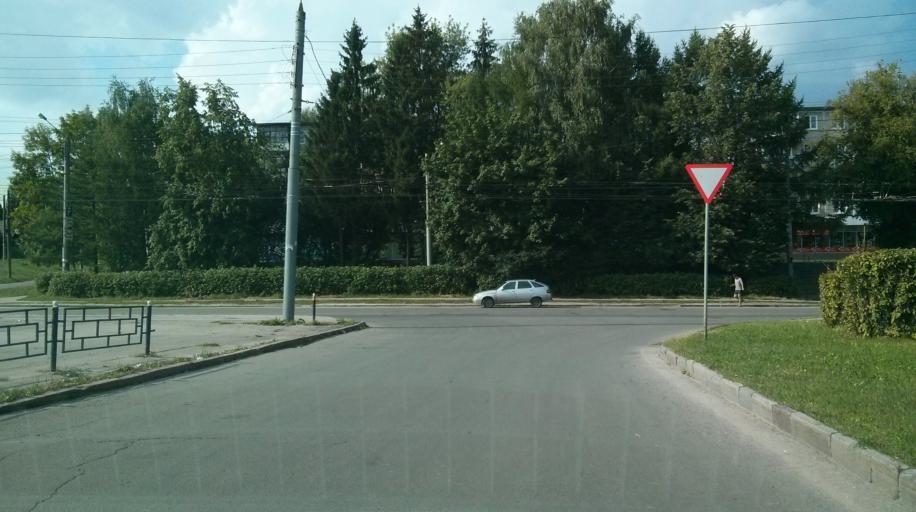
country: RU
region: Nizjnij Novgorod
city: Nizhniy Novgorod
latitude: 56.2967
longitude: 44.0348
